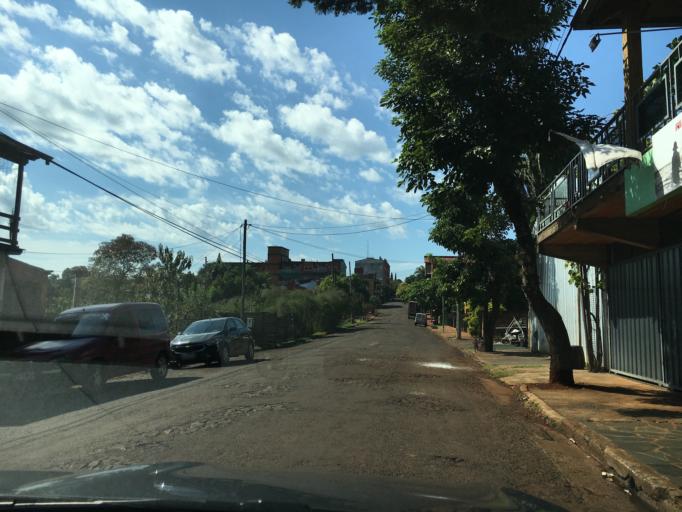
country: AR
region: Misiones
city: Puerto Rico
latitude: -26.8204
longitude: -55.0295
